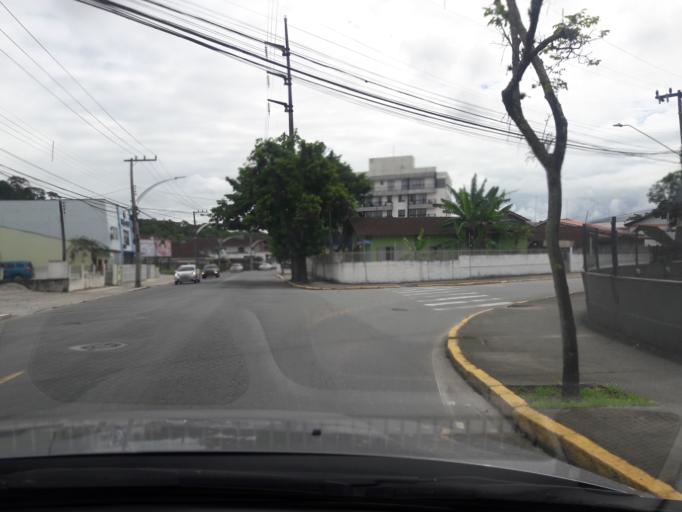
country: BR
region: Santa Catarina
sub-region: Joinville
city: Joinville
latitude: -26.3232
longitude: -48.8547
